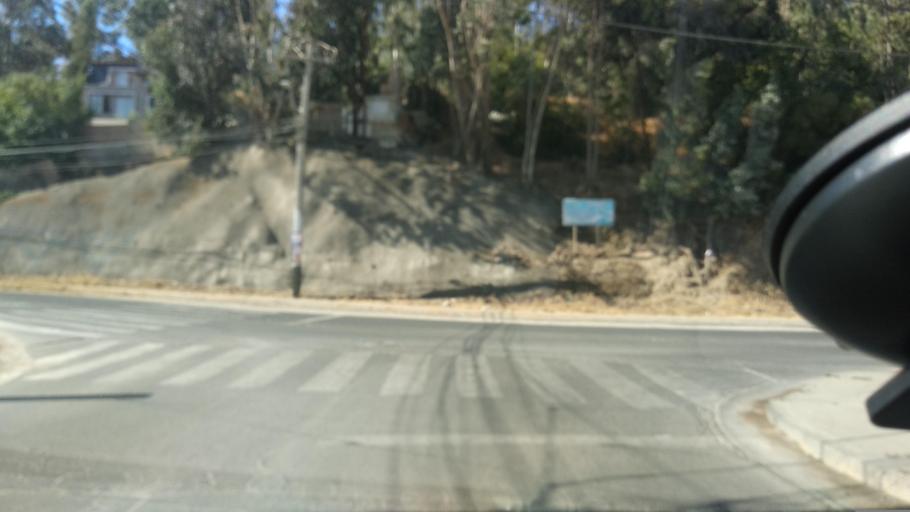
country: CL
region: Valparaiso
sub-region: Provincia de Marga Marga
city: Villa Alemana
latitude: -33.0389
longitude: -71.3903
